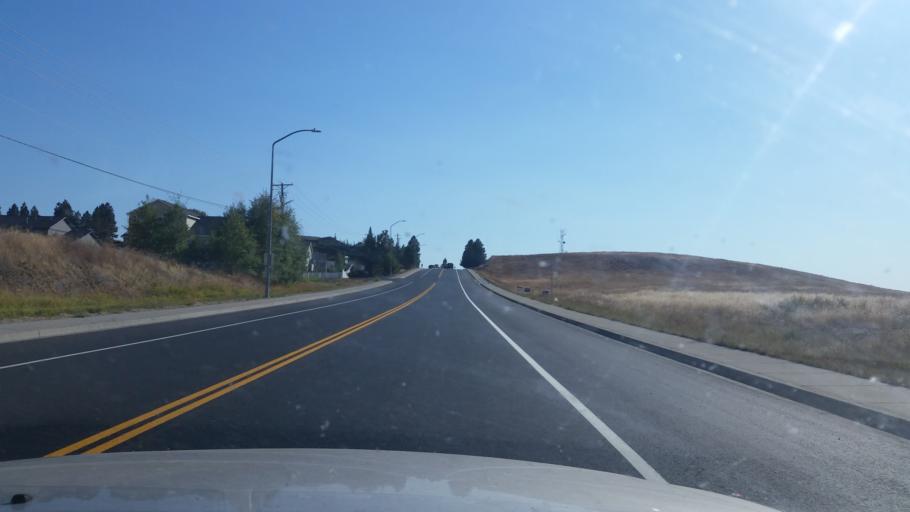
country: US
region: Washington
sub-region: Spokane County
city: Cheney
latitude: 47.5026
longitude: -117.5864
